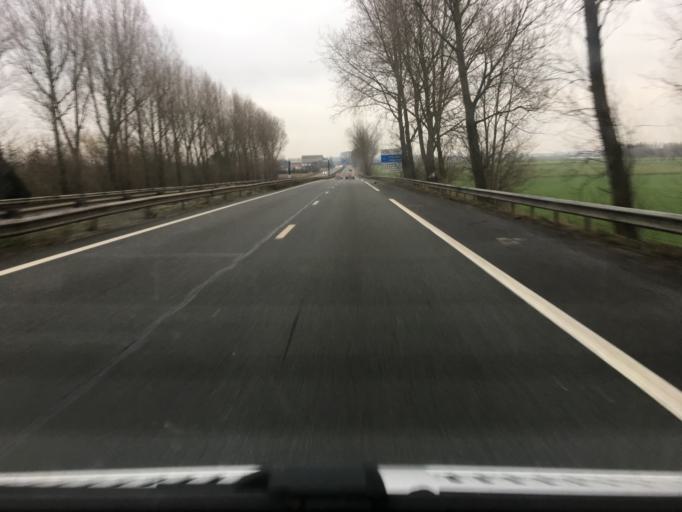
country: FR
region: Nord-Pas-de-Calais
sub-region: Departement du Nord
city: Bierne
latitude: 50.9696
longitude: 2.3959
